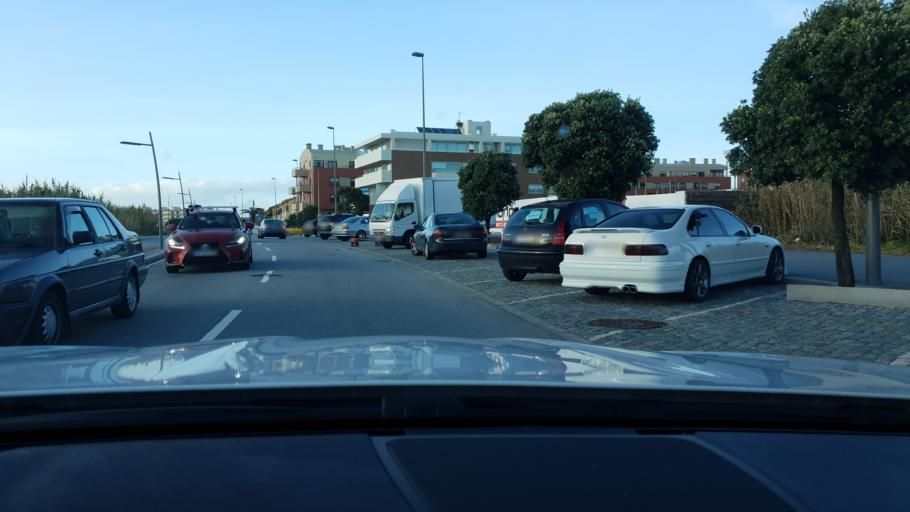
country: PT
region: Porto
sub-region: Matosinhos
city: Santa Cruz do Bispo
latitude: 41.2224
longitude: -8.7146
